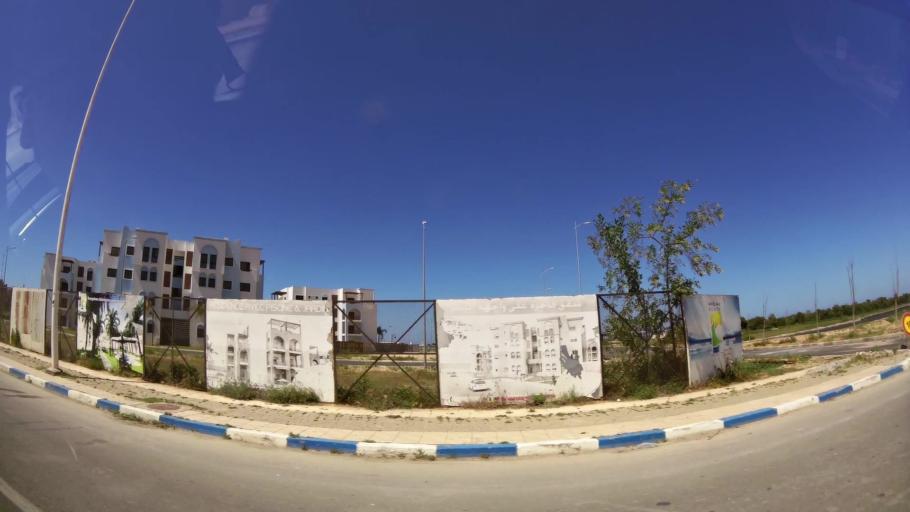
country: MA
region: Oriental
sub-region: Berkane-Taourirt
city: Madagh
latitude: 35.1382
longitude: -2.4203
